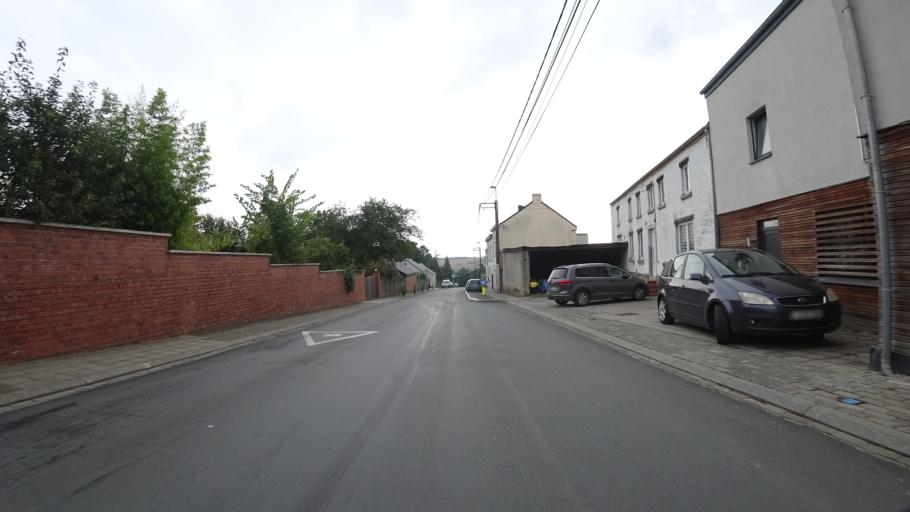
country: BE
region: Wallonia
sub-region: Province du Brabant Wallon
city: Mont-Saint-Guibert
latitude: 50.6393
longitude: 4.6096
